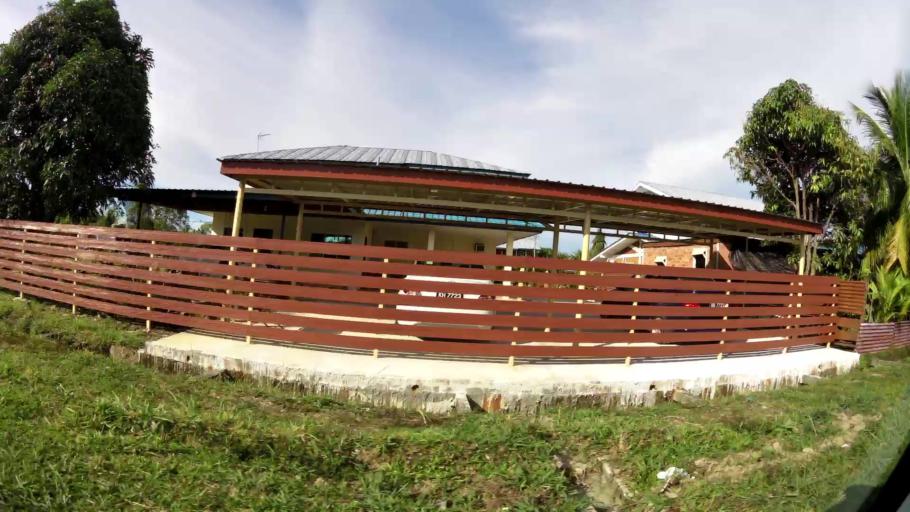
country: BN
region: Brunei and Muara
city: Bandar Seri Begawan
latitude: 4.9687
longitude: 115.0262
